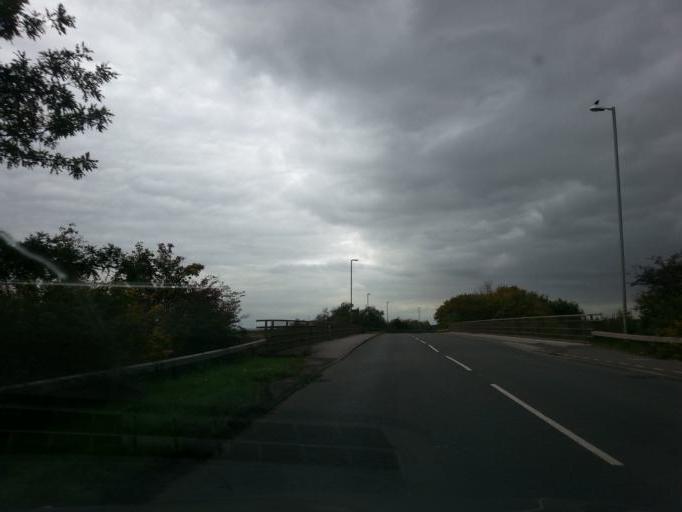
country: GB
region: England
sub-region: Nottinghamshire
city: Newark on Trent
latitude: 53.0462
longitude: -0.7770
